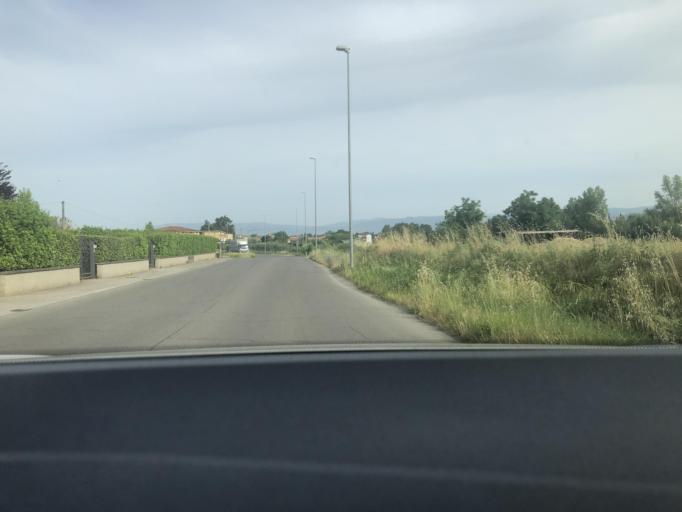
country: IT
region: Tuscany
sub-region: Provincia di Pistoia
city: San Rocco
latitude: 43.8126
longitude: 10.8641
